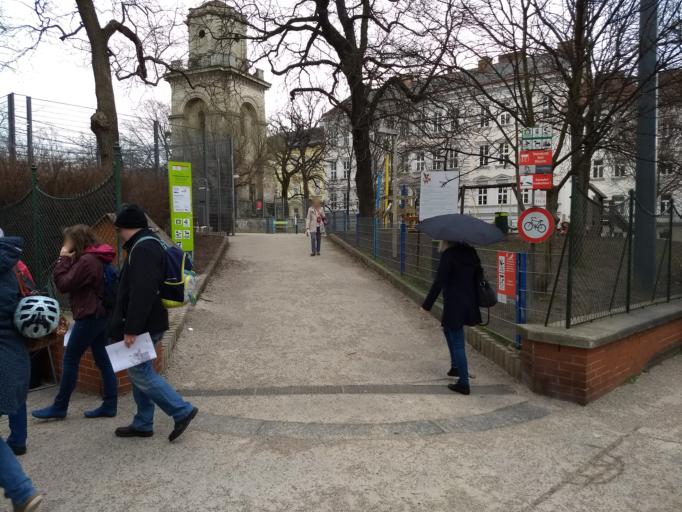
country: AT
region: Vienna
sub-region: Wien Stadt
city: Vienna
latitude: 48.2211
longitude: 16.3422
